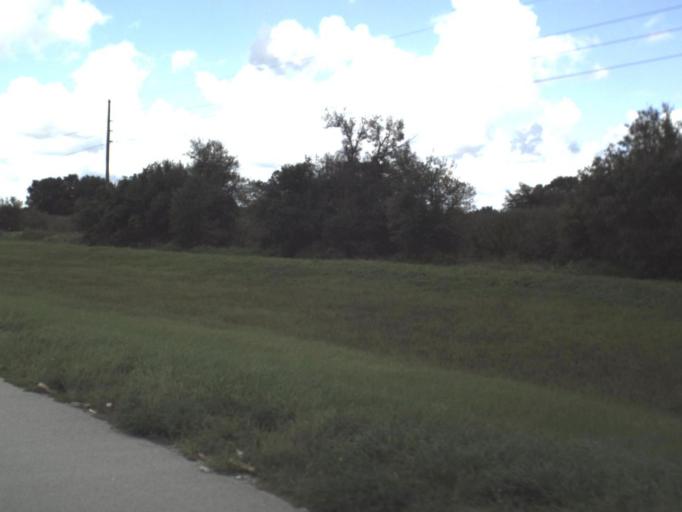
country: US
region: Florida
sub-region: DeSoto County
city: Southeast Arcadia
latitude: 27.2096
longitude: -81.6469
